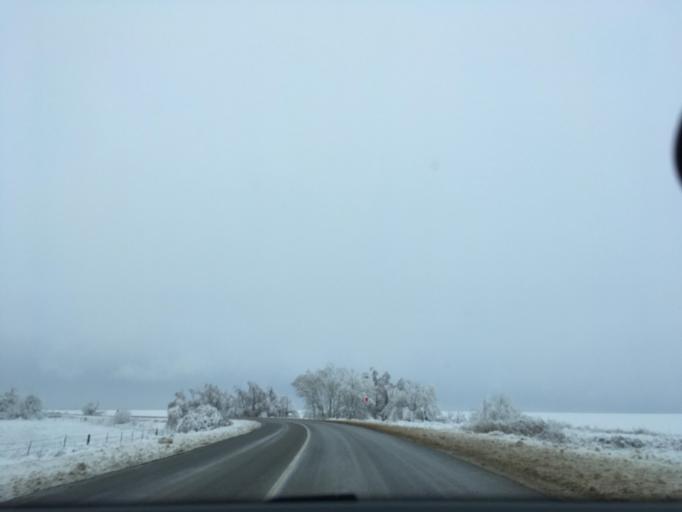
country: RU
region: Voronezj
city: Ol'khovatka
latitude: 50.2210
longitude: 39.2742
